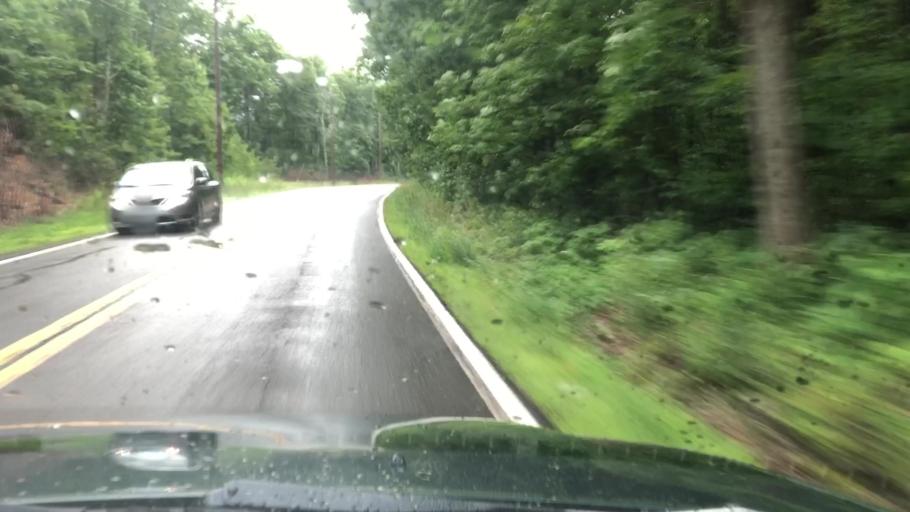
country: US
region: Pennsylvania
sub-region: Wayne County
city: Hawley
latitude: 41.3425
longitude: -75.2101
